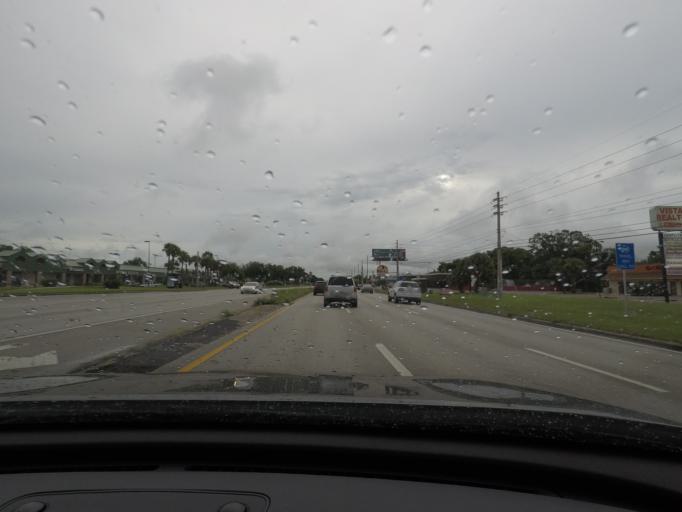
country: US
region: Florida
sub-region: Orange County
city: Azalea Park
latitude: 28.5533
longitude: -81.3238
